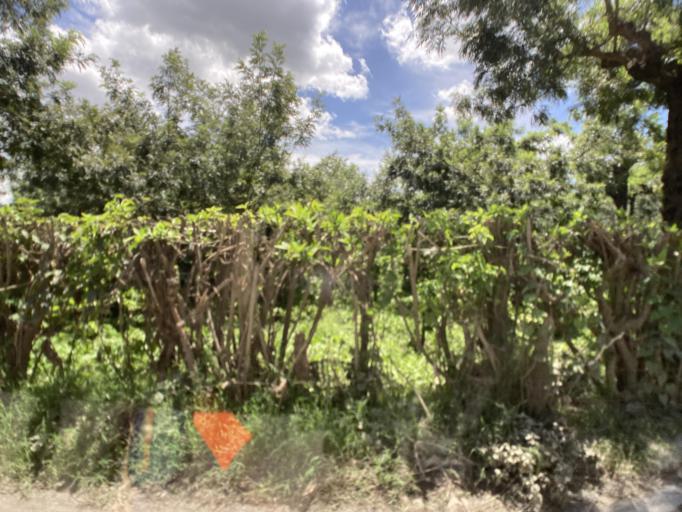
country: GT
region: Sacatepequez
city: Antigua Guatemala
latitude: 14.5405
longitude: -90.7354
